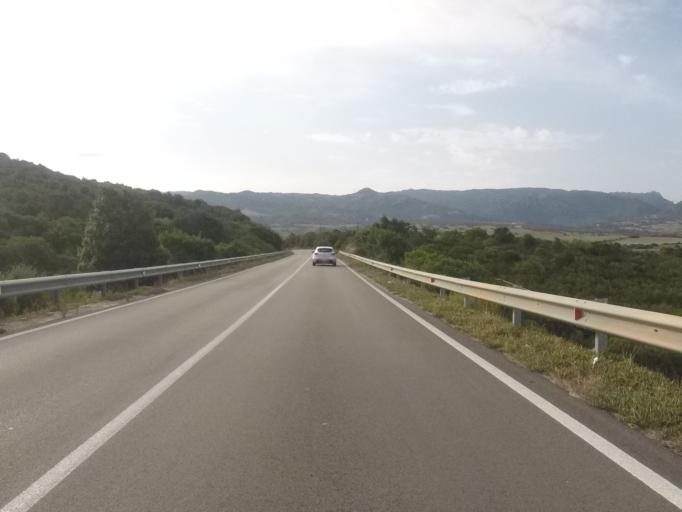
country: IT
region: Sardinia
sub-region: Provincia di Olbia-Tempio
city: Aglientu
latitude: 41.1082
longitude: 9.0621
